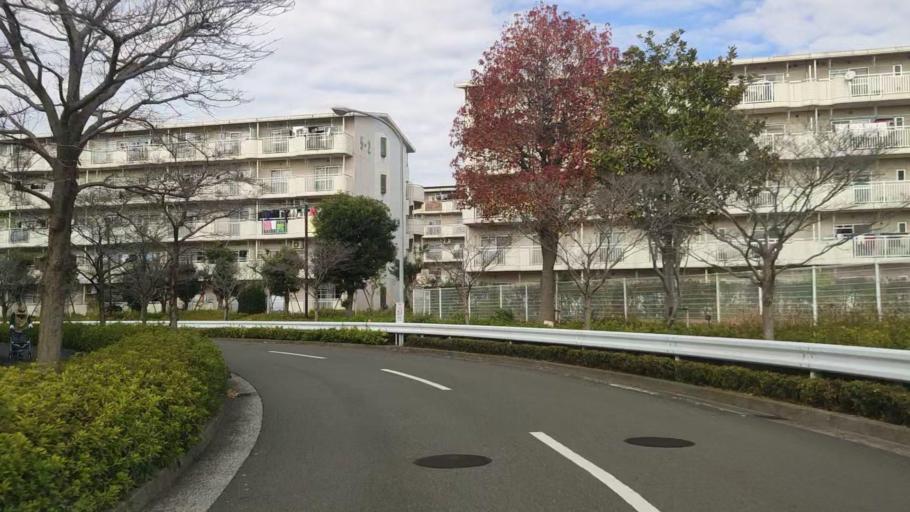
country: JP
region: Kanagawa
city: Minami-rinkan
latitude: 35.4828
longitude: 139.4905
